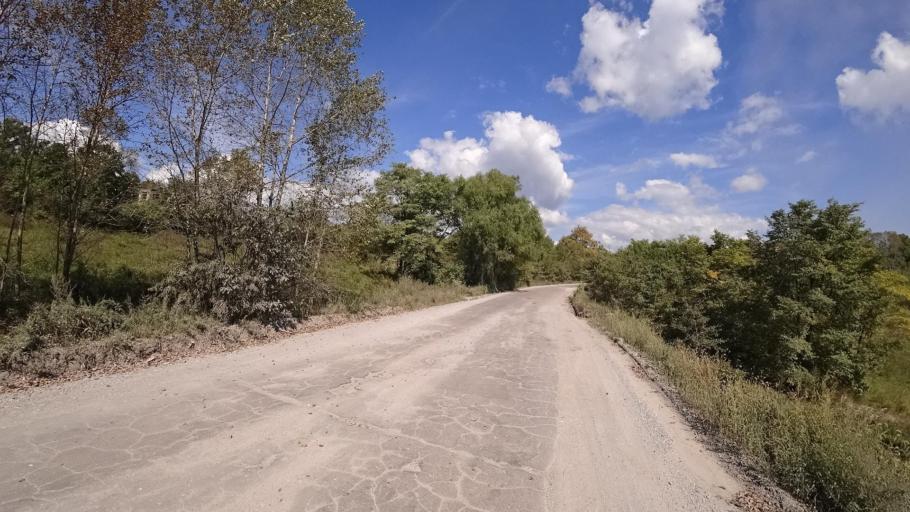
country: RU
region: Jewish Autonomous Oblast
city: Londoko
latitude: 49.0098
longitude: 131.8954
